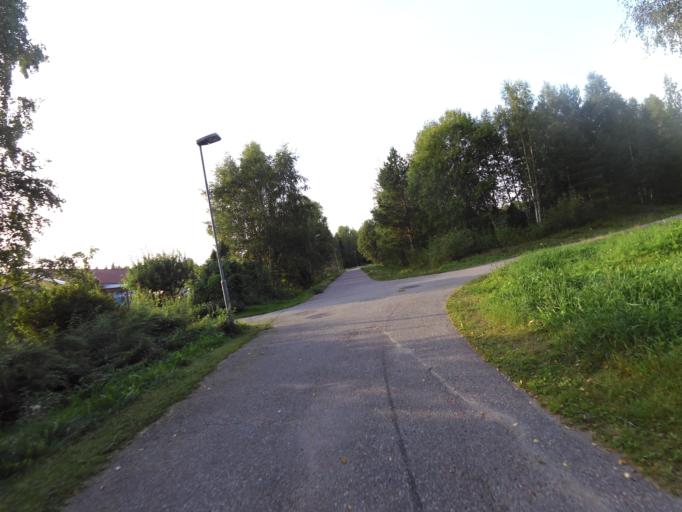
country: SE
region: Gaevleborg
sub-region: Gavle Kommun
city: Gavle
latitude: 60.6991
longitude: 17.0982
